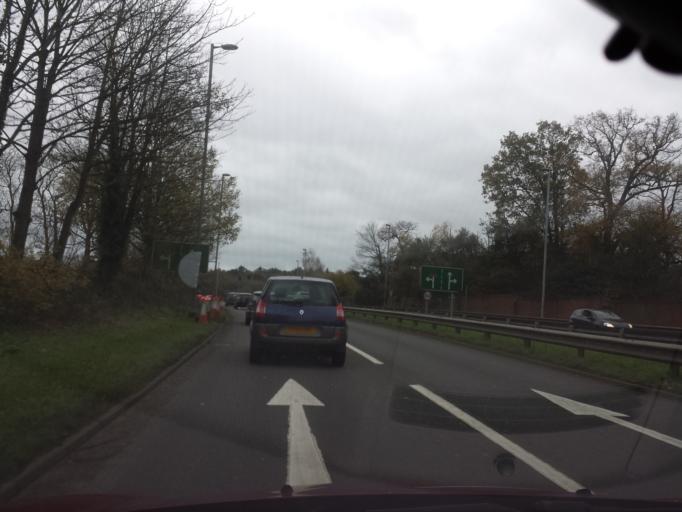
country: GB
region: England
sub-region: Surrey
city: Bagshot
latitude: 51.3579
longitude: -0.6831
